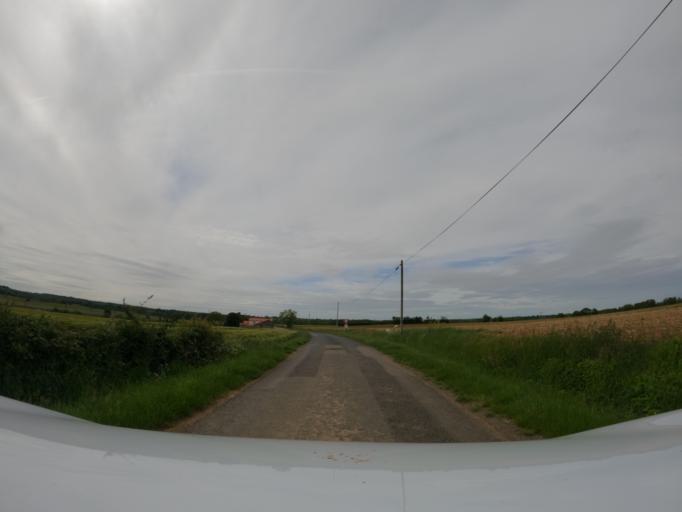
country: FR
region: Pays de la Loire
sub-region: Departement de la Vendee
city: Saint-Hilaire-des-Loges
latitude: 46.5034
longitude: -0.6463
